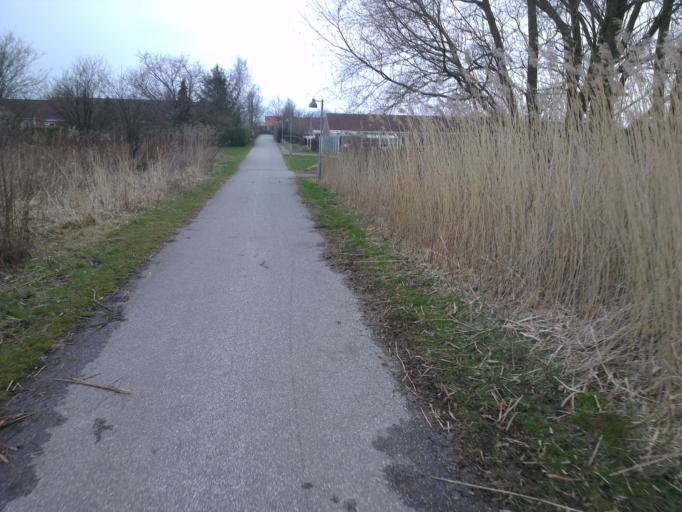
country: DK
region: Capital Region
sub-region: Frederikssund Kommune
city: Frederikssund
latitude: 55.8589
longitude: 12.0820
